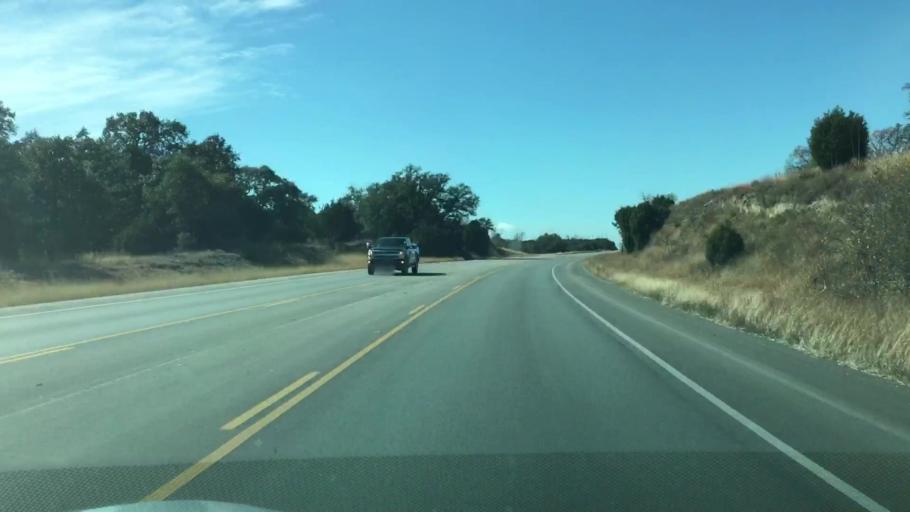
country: US
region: Texas
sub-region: Hays County
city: Dripping Springs
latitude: 30.2072
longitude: -98.1450
